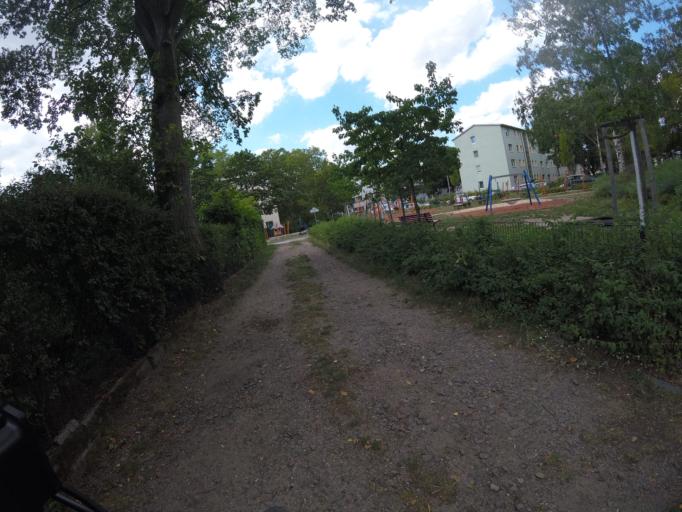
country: DE
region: Berlin
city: Haselhorst
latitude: 52.5407
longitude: 13.2426
